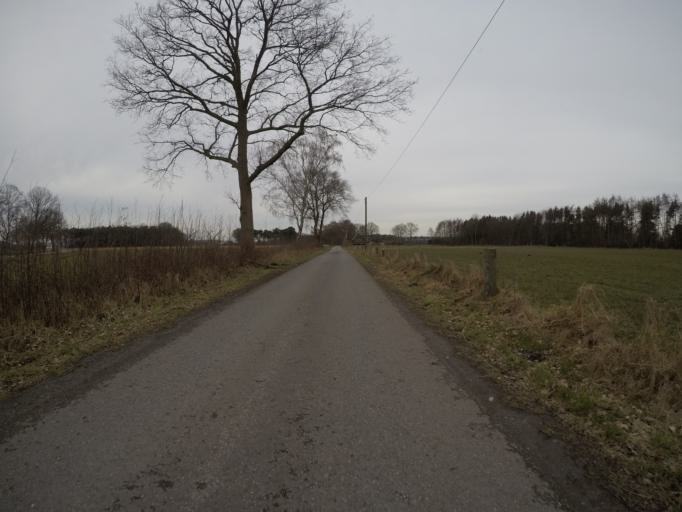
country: DE
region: North Rhine-Westphalia
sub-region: Regierungsbezirk Dusseldorf
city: Bocholt
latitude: 51.7993
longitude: 6.6341
